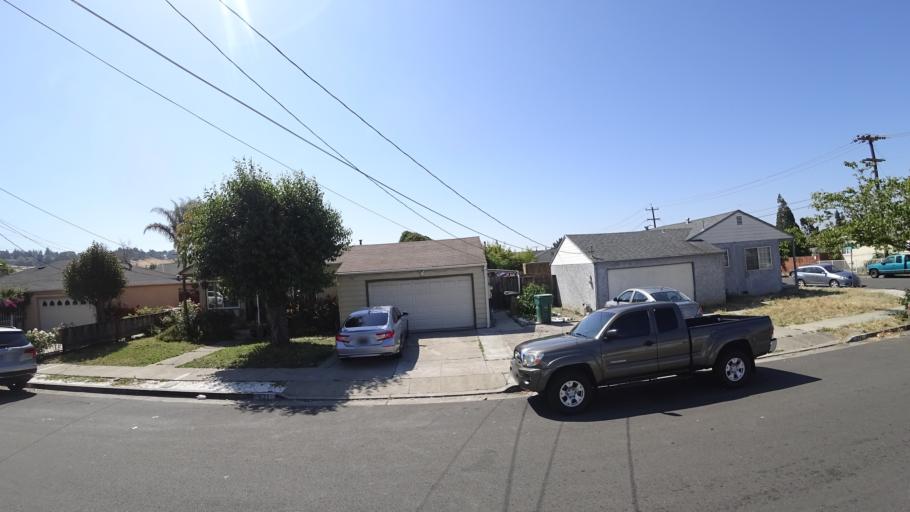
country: US
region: California
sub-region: Alameda County
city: Hayward
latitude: 37.6609
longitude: -122.0794
